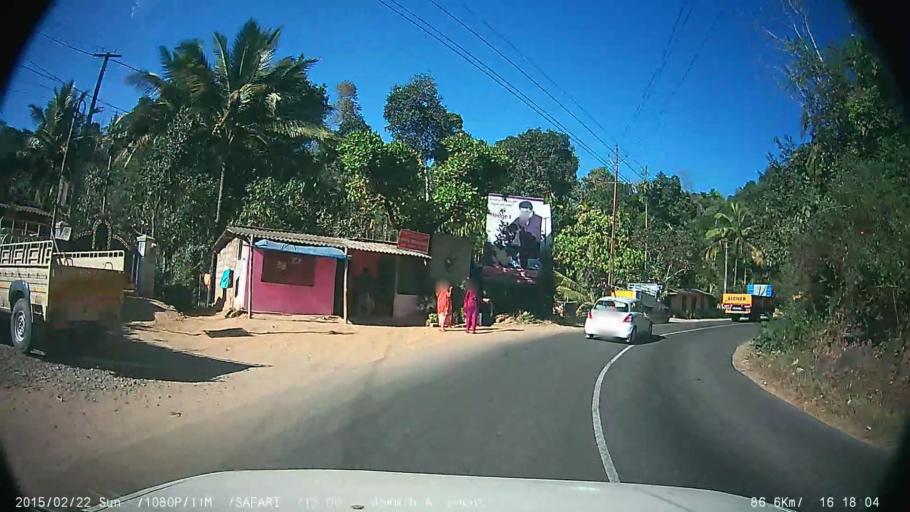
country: IN
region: Tamil Nadu
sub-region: Theni
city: Gudalur
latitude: 9.5847
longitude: 77.1197
